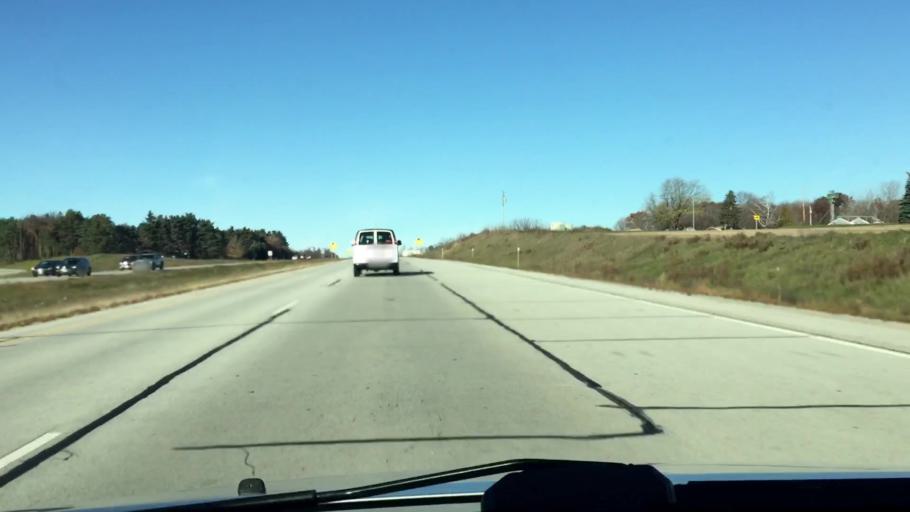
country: US
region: Wisconsin
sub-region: Brown County
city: Howard
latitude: 44.5638
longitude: -88.1381
